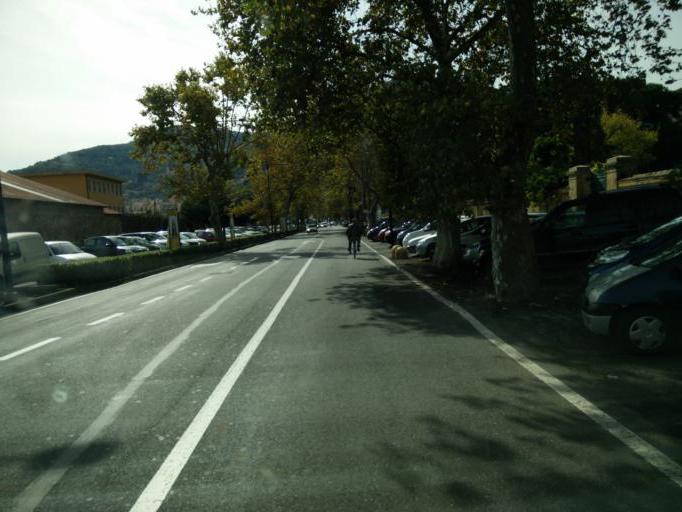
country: IT
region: Liguria
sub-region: Provincia di La Spezia
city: La Spezia
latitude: 44.1055
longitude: 9.8133
